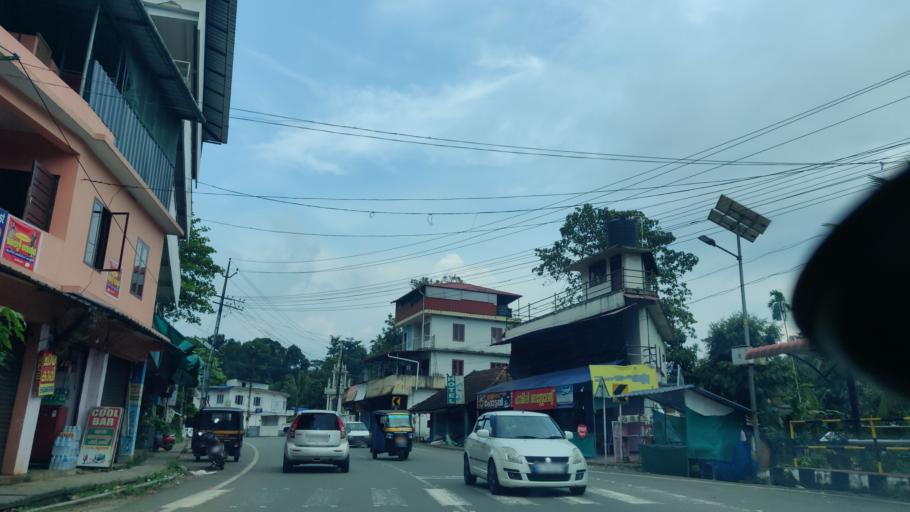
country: IN
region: Kerala
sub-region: Kottayam
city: Palackattumala
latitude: 9.8579
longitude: 76.6910
